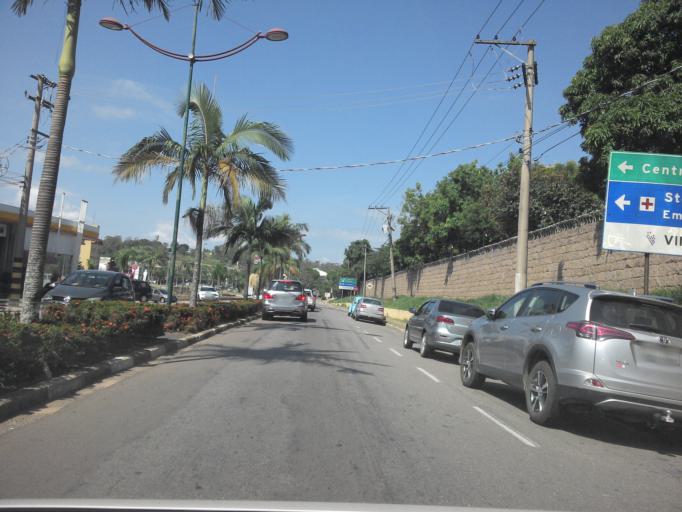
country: BR
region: Sao Paulo
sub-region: Vinhedo
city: Vinhedo
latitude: -23.0382
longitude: -46.9855
